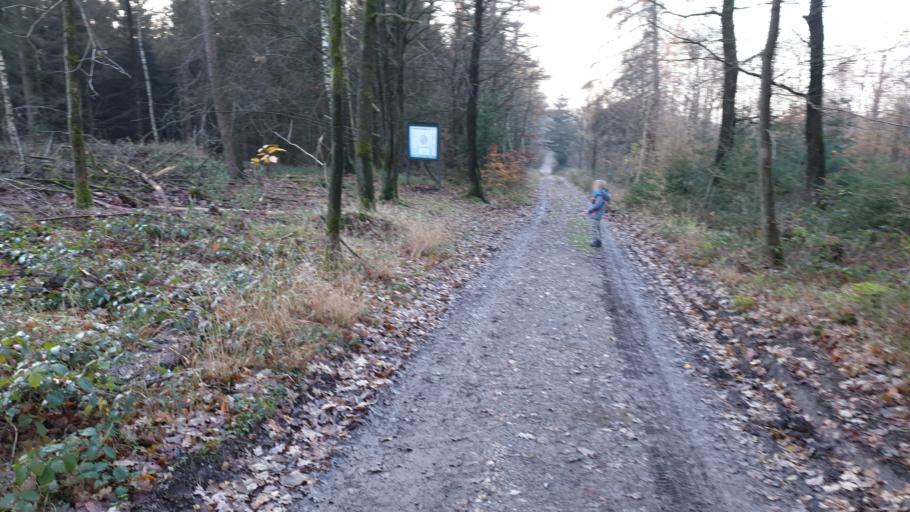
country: DE
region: North Rhine-Westphalia
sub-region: Regierungsbezirk Detmold
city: Horn-Bad Meinberg
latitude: 51.9226
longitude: 8.9534
